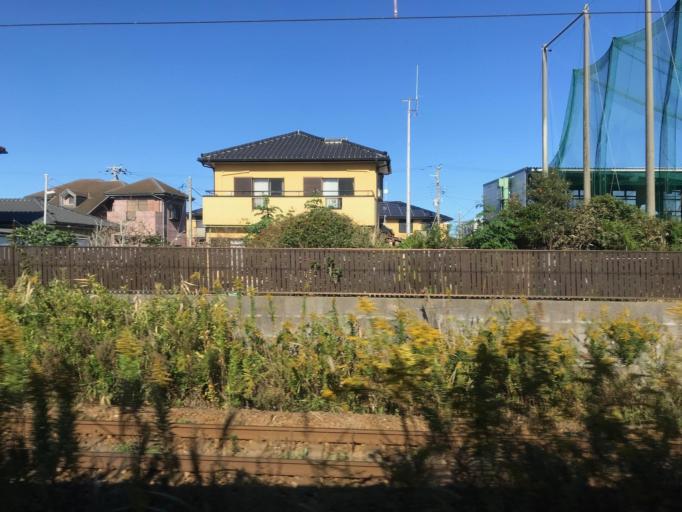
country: JP
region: Chiba
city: Hasaki
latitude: 35.7439
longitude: 140.7851
